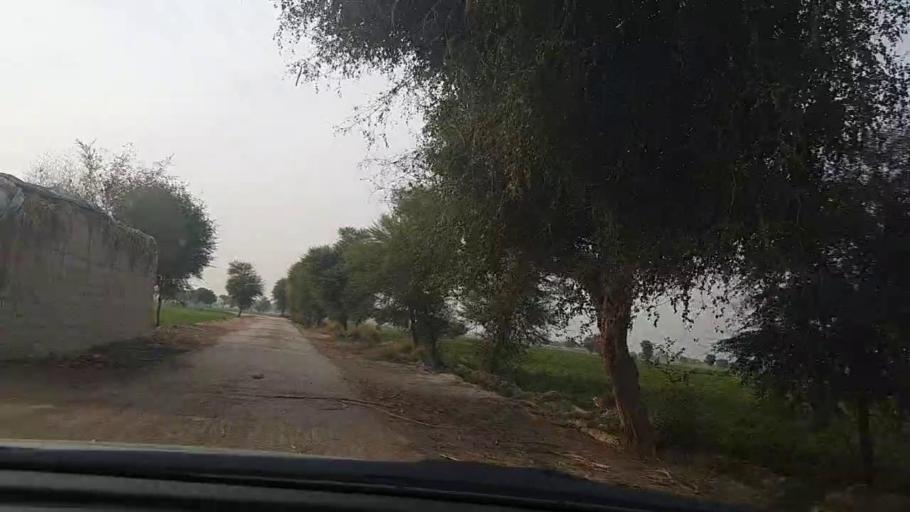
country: PK
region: Sindh
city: Daulatpur
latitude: 26.3358
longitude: 68.0379
